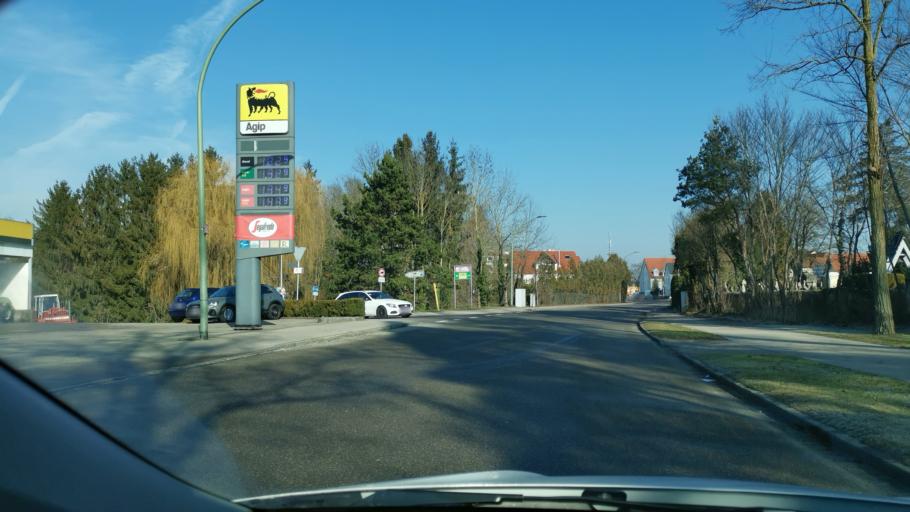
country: DE
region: Bavaria
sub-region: Swabia
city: Rain
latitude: 48.6875
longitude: 10.9199
